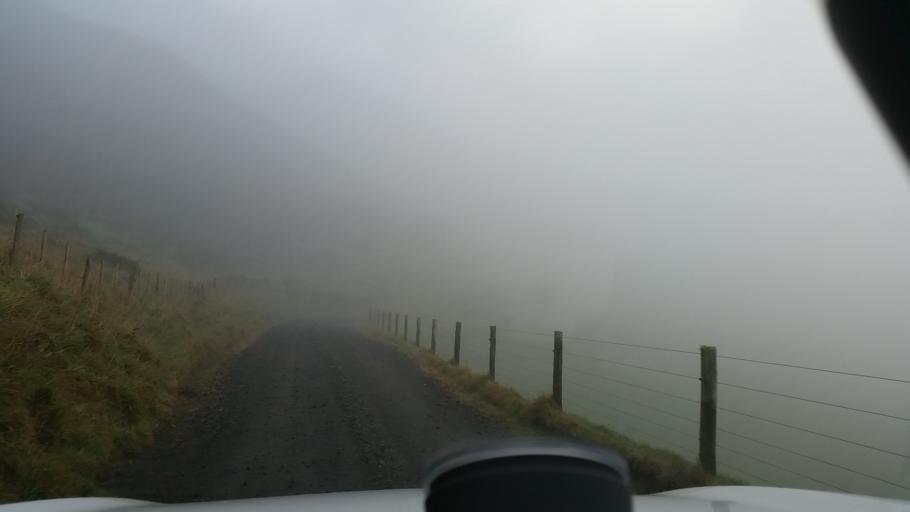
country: NZ
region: Taranaki
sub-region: South Taranaki District
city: Eltham
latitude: -39.4100
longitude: 174.4283
